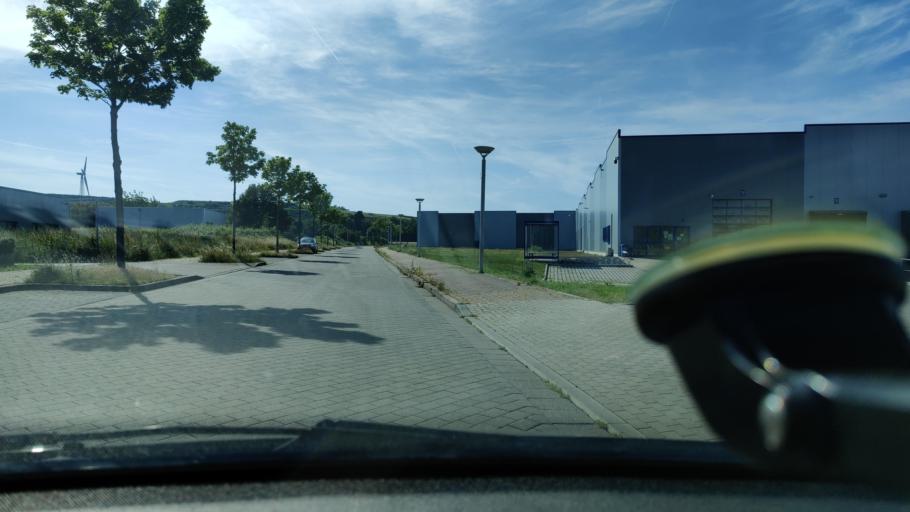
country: DE
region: North Rhine-Westphalia
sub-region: Regierungsbezirk Dusseldorf
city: Kamp-Lintfort
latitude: 51.4813
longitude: 6.5338
